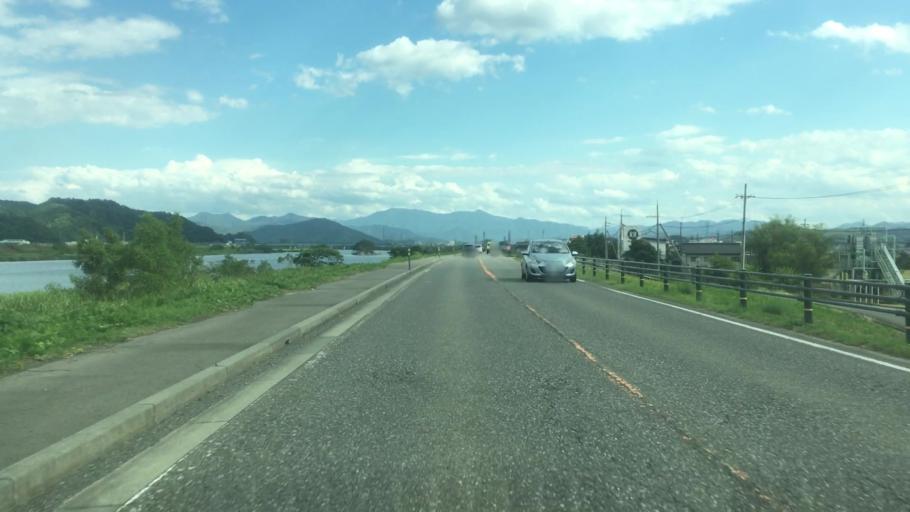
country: JP
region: Hyogo
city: Toyooka
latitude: 35.5711
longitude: 134.8082
